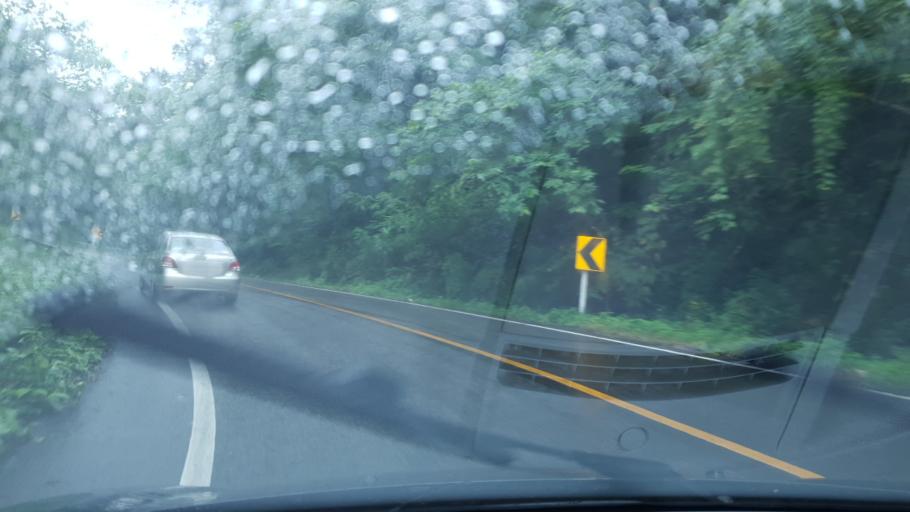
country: TH
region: Mae Hong Son
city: Khun Yuam
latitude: 18.6717
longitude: 97.9259
